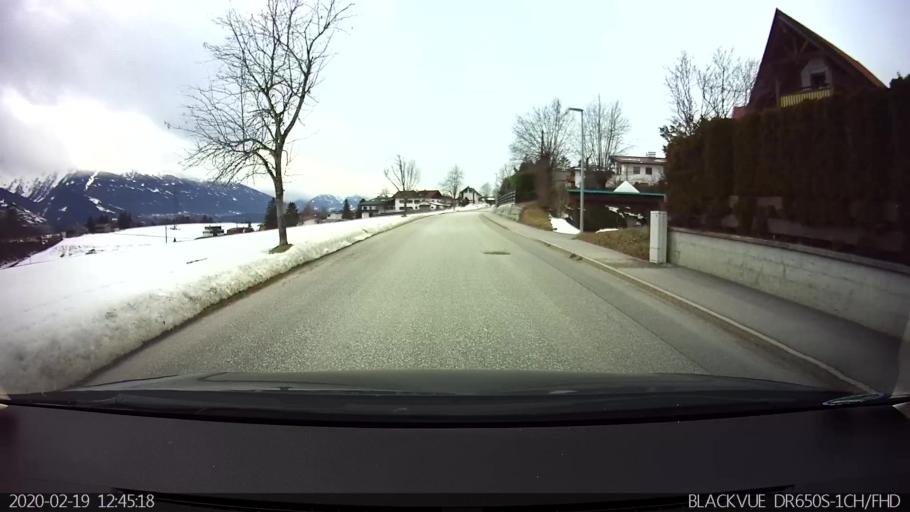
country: AT
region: Tyrol
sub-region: Politischer Bezirk Innsbruck Land
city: Fritzens
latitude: 47.3234
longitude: 11.5909
